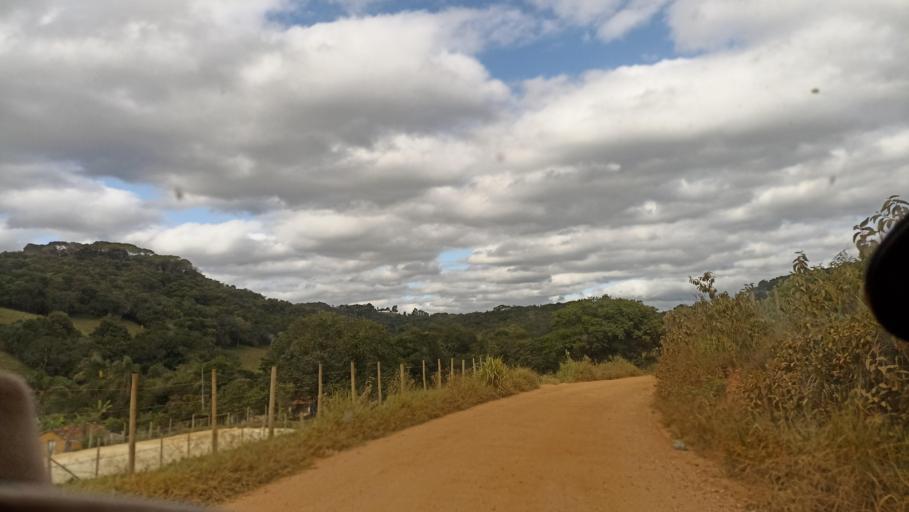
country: BR
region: Minas Gerais
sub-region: Tiradentes
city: Tiradentes
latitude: -21.1017
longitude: -44.1081
